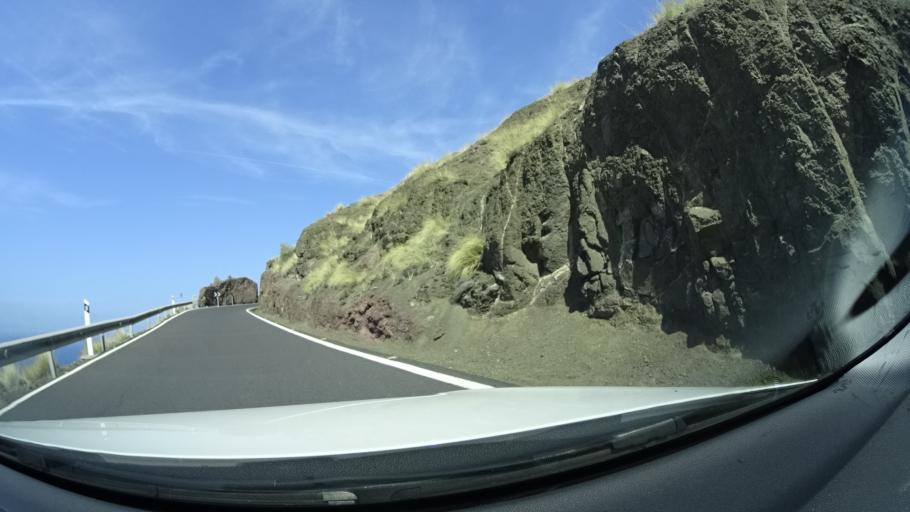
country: ES
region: Canary Islands
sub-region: Provincia de Las Palmas
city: Agaete
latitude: 28.0874
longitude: -15.7038
